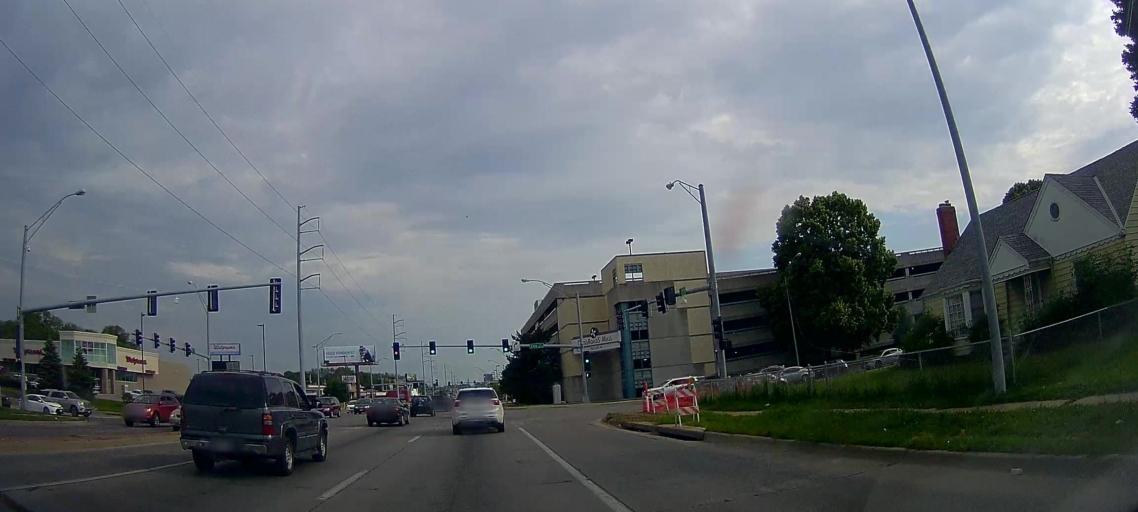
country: US
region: Nebraska
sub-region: Douglas County
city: Ralston
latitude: 41.2637
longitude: -96.0240
